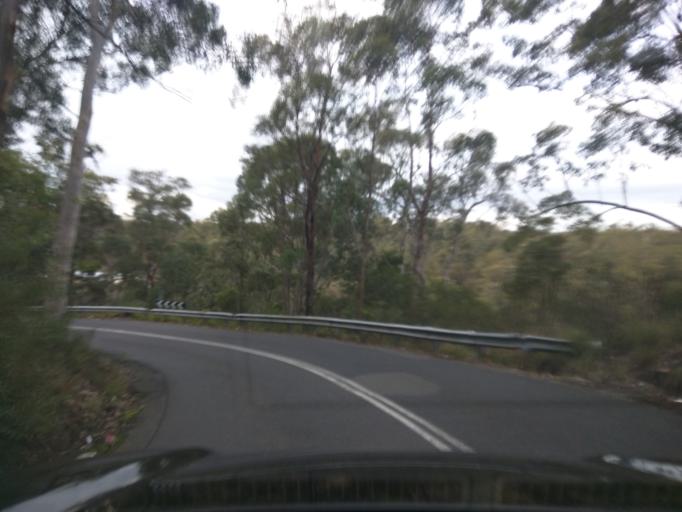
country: AU
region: New South Wales
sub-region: Wollondilly
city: Douglas Park
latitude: -34.2297
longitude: 150.7416
